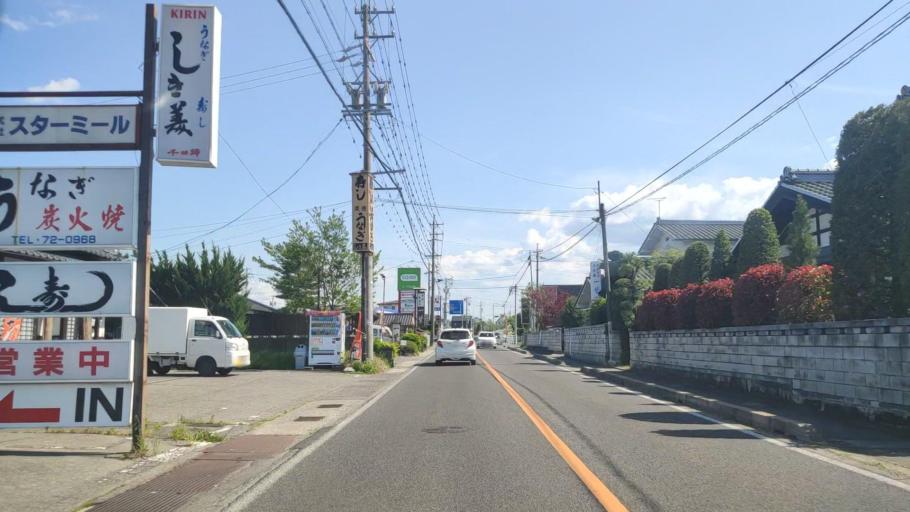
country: JP
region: Nagano
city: Toyoshina
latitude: 36.2874
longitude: 137.9078
